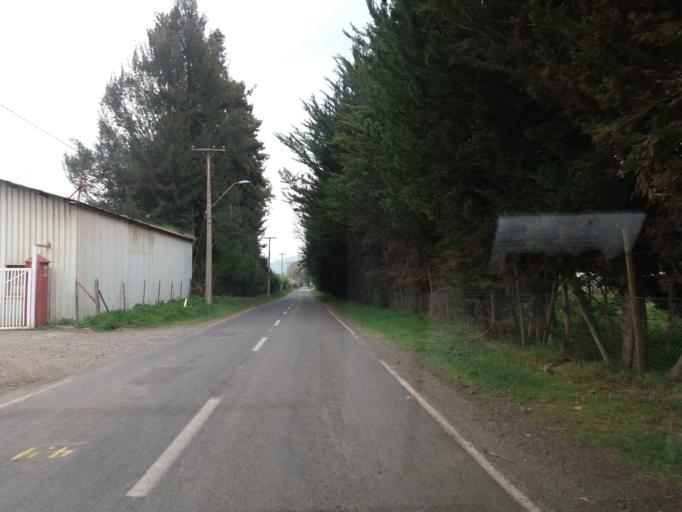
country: CL
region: Valparaiso
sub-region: Provincia de Quillota
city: Quillota
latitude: -32.8873
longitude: -71.1085
